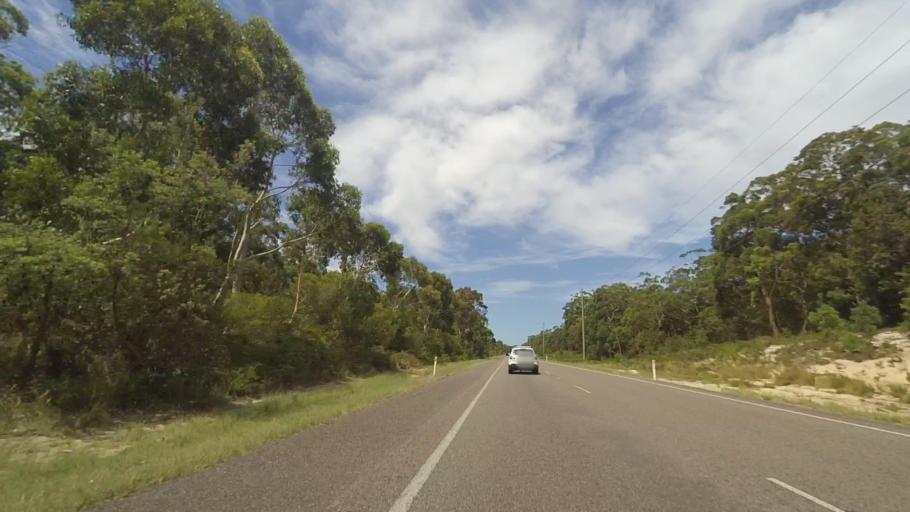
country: AU
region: New South Wales
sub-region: Port Stephens Shire
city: Medowie
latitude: -32.7904
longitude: 151.9572
